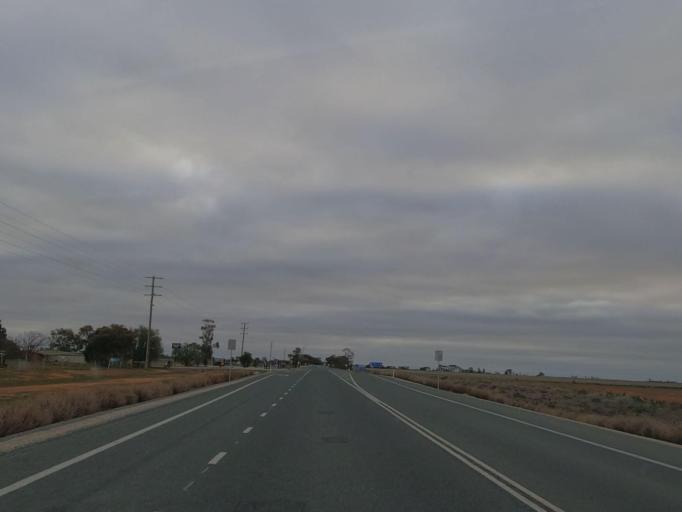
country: AU
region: Victoria
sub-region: Swan Hill
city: Swan Hill
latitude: -35.5525
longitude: 143.7720
